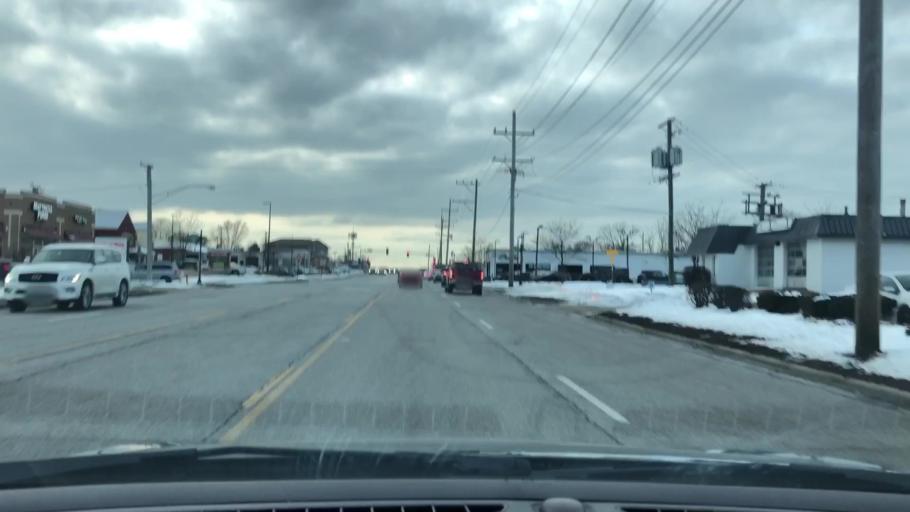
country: US
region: Illinois
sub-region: DuPage County
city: Downers Grove
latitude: 41.8097
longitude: -87.9923
